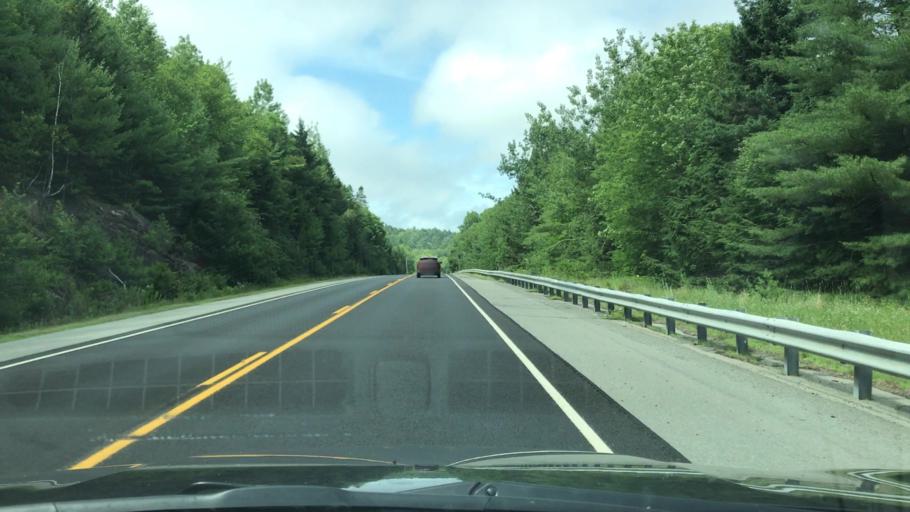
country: US
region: Maine
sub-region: Hancock County
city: Bucksport
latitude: 44.5500
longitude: -68.8096
